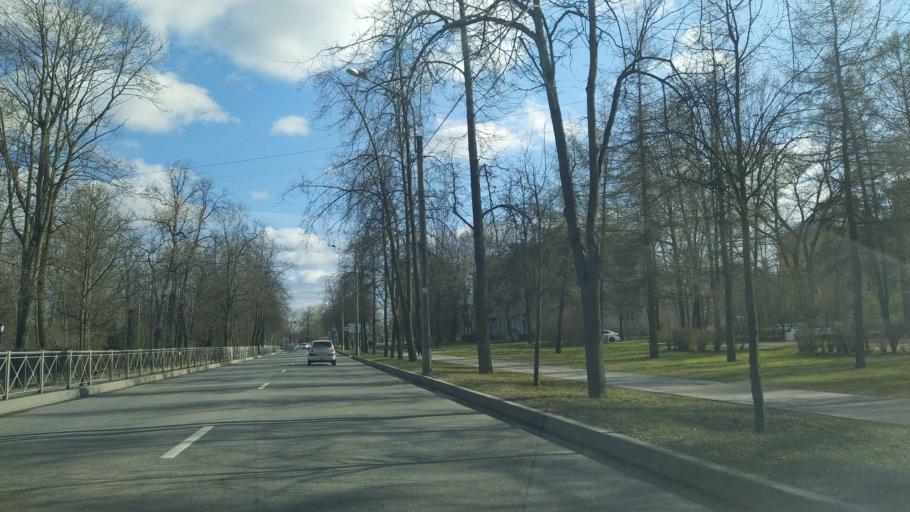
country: RU
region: St.-Petersburg
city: Pushkin
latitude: 59.7052
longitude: 30.4180
